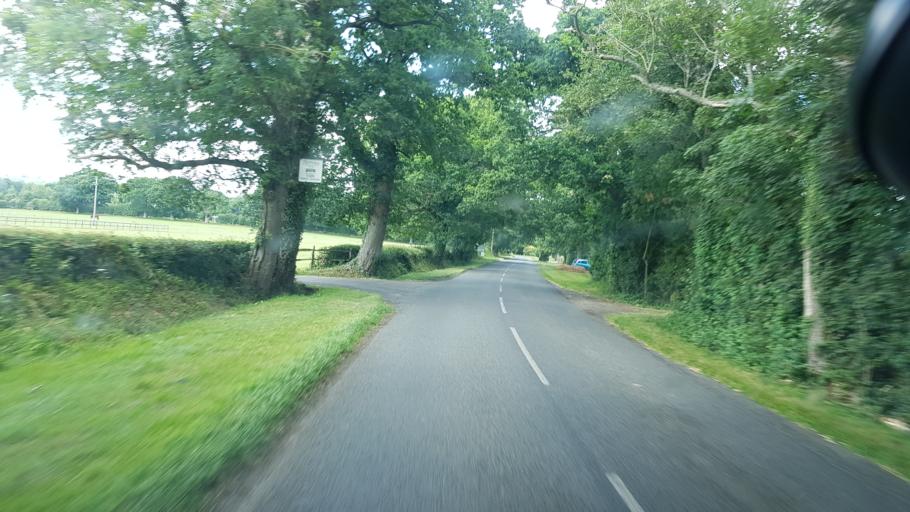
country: GB
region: England
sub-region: West Sussex
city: Rudgwick
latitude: 51.0787
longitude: -0.4535
